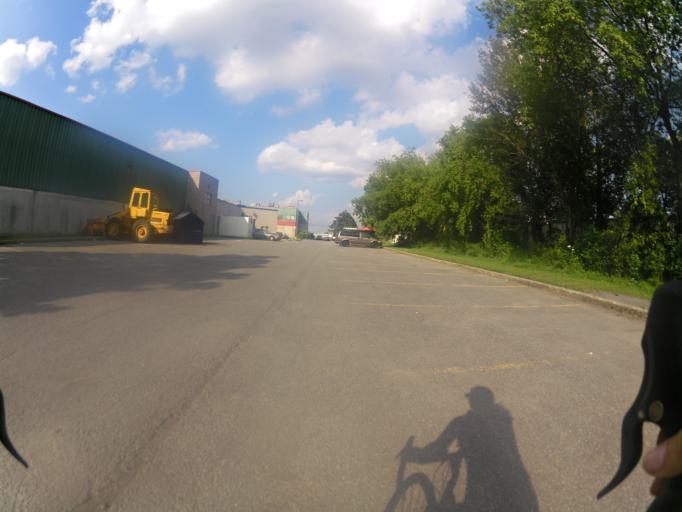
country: CA
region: Ontario
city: Ottawa
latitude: 45.3281
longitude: -75.7223
